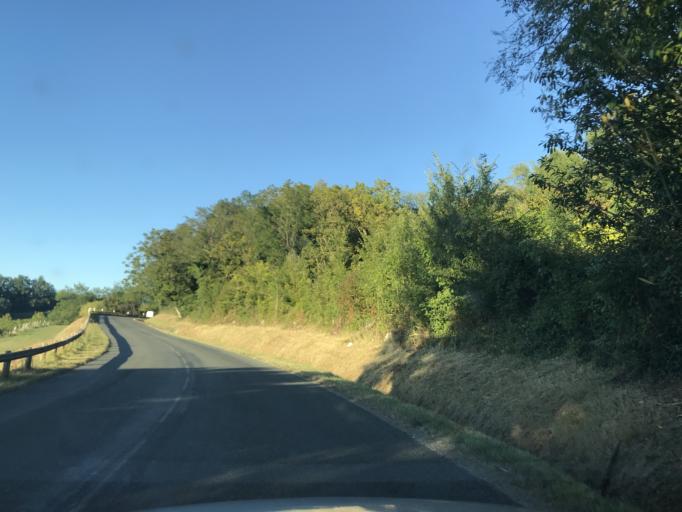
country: FR
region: Aquitaine
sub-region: Departement de la Gironde
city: Mouliets-et-Villemartin
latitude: 44.8805
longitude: -0.0471
